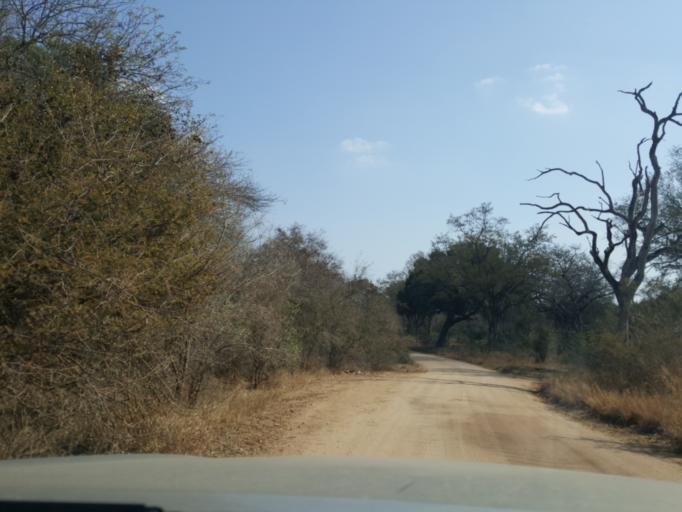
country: ZA
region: Mpumalanga
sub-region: Ehlanzeni District
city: Komatipoort
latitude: -25.2906
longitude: 31.7652
